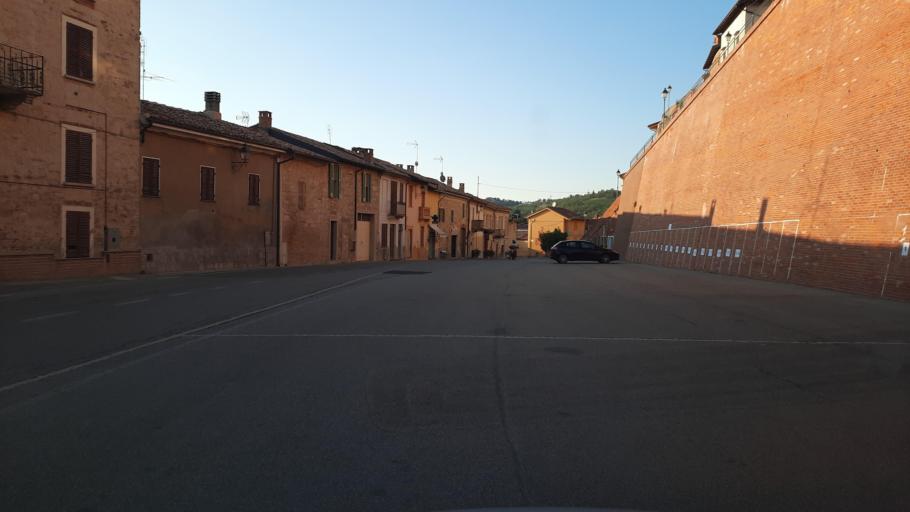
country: IT
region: Piedmont
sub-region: Provincia di Asti
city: Grazzano Badoglio
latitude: 45.0391
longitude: 8.3131
